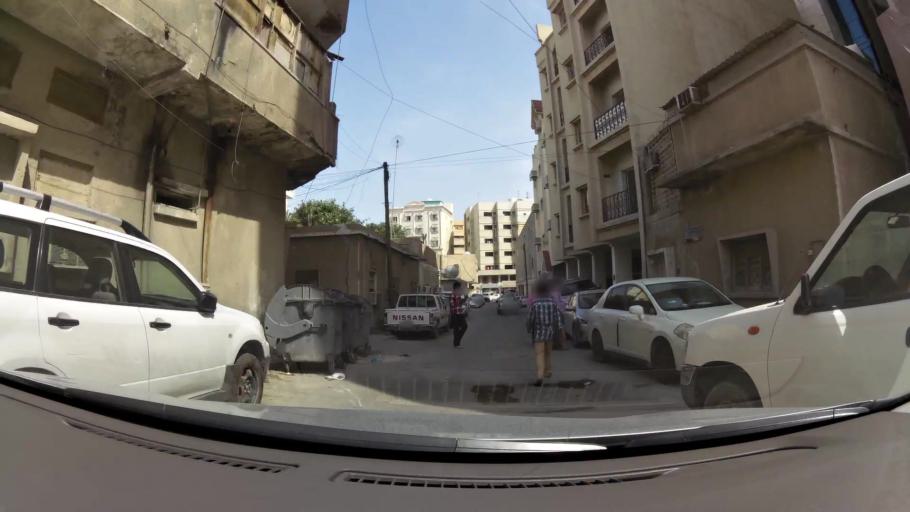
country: QA
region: Baladiyat ad Dawhah
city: Doha
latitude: 25.2810
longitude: 51.5303
